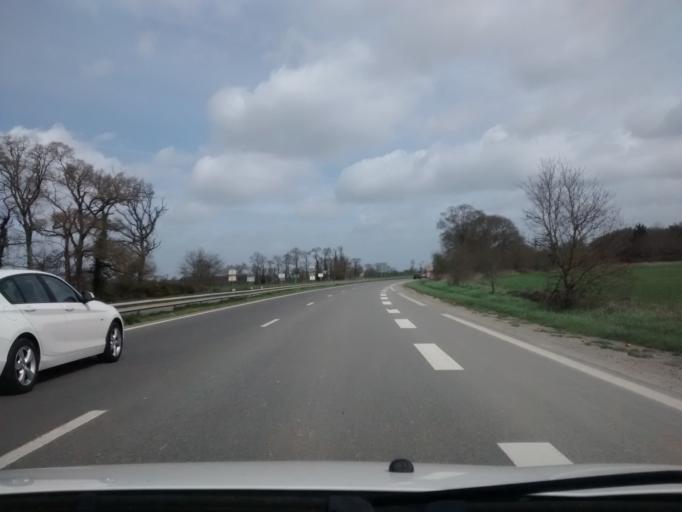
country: FR
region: Brittany
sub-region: Departement d'Ille-et-Vilaine
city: Bruz
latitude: 48.0473
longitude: -1.7524
